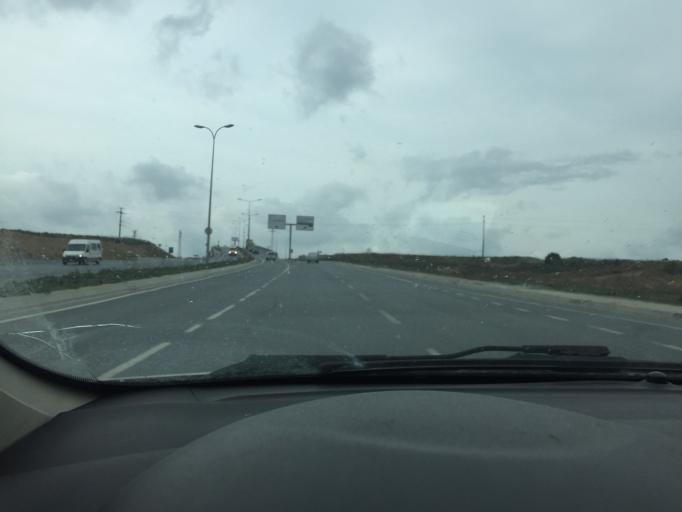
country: TR
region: Istanbul
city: Basaksehir
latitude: 41.1411
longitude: 28.7959
